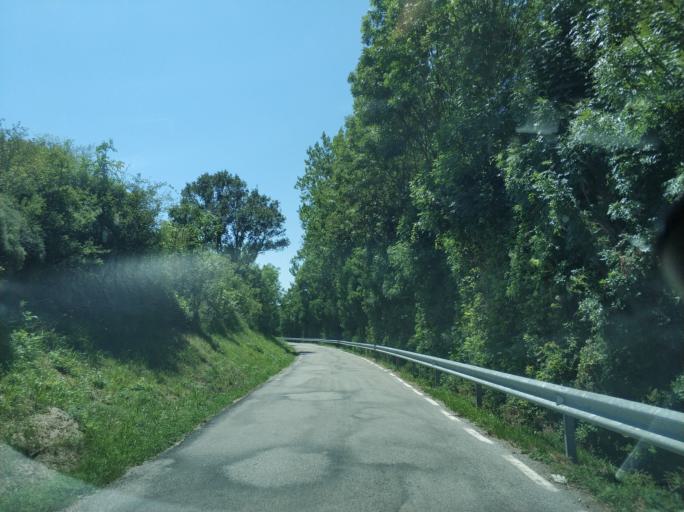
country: ES
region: Cantabria
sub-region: Provincia de Cantabria
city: Reinosa
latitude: 43.0124
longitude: -4.1648
